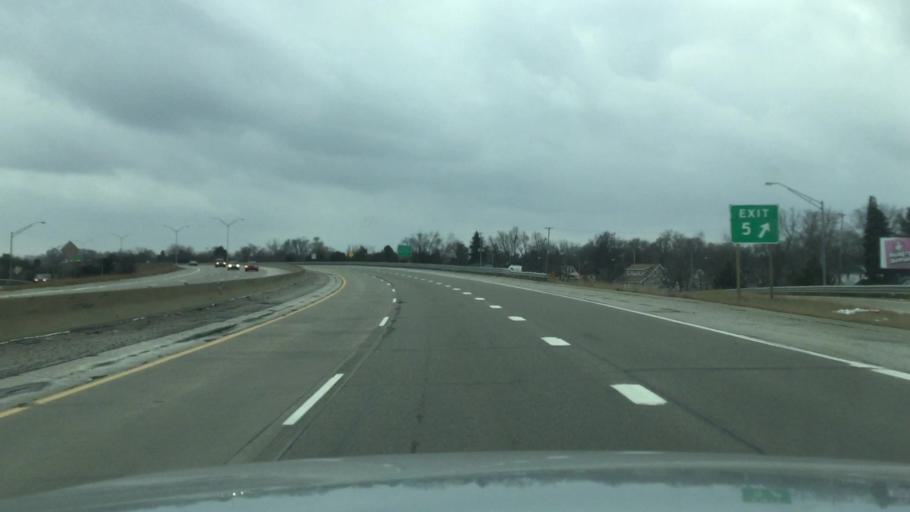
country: US
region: Michigan
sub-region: Genesee County
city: Flint
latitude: 42.9921
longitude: -83.6816
